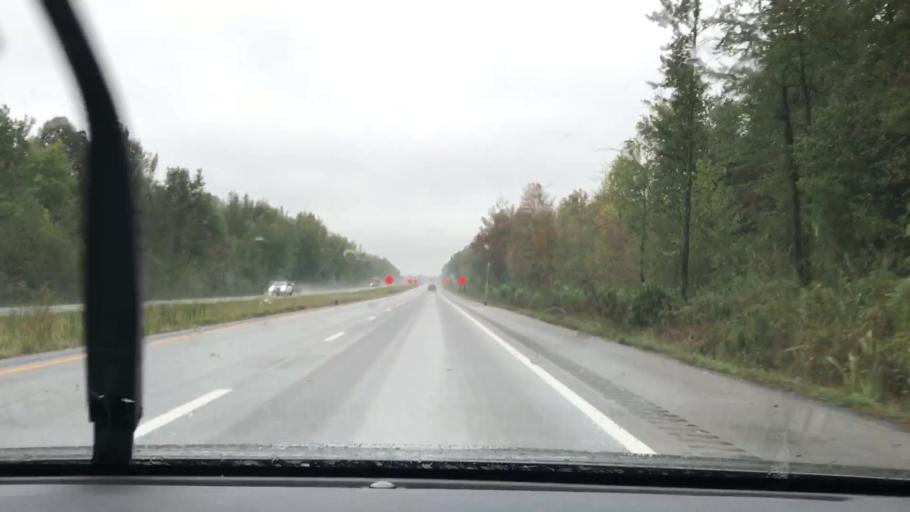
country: US
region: Kentucky
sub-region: Hopkins County
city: Nortonville
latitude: 37.1633
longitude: -87.4562
